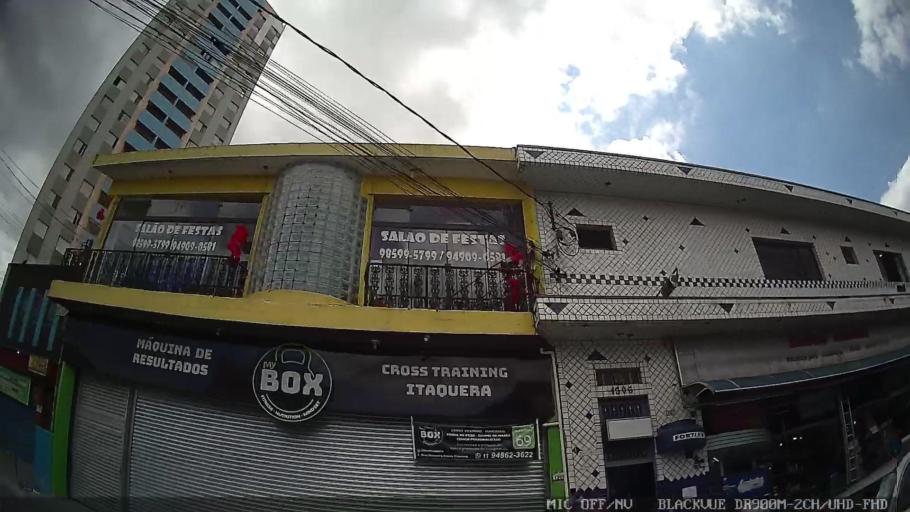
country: BR
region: Sao Paulo
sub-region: Ferraz De Vasconcelos
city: Ferraz de Vasconcelos
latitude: -23.5340
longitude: -46.4634
